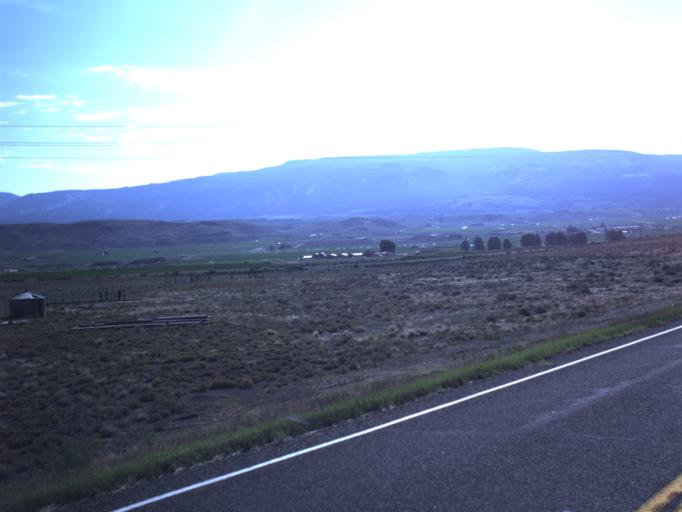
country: US
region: Utah
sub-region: Wayne County
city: Loa
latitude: 38.4146
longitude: -111.6480
